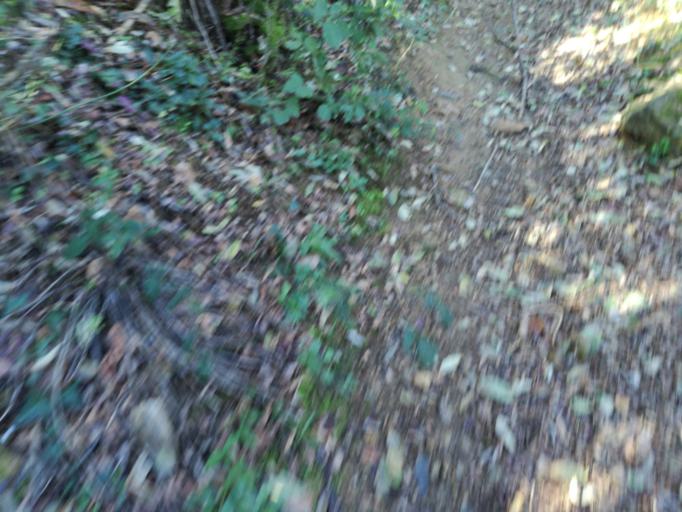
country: IT
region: Veneto
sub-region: Provincia di Padova
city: Arqua Petrarca
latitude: 45.2801
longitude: 11.7362
